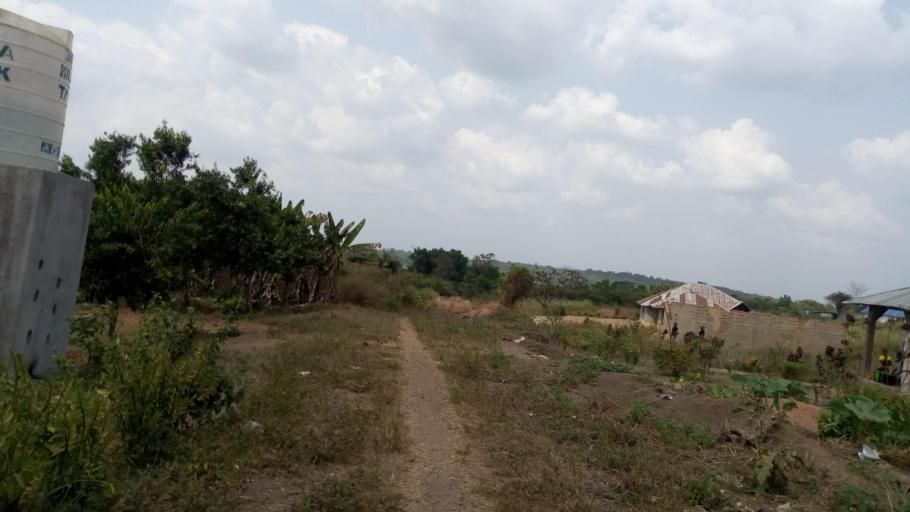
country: SL
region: Southern Province
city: Mogbwemo
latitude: 7.7896
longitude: -12.3086
